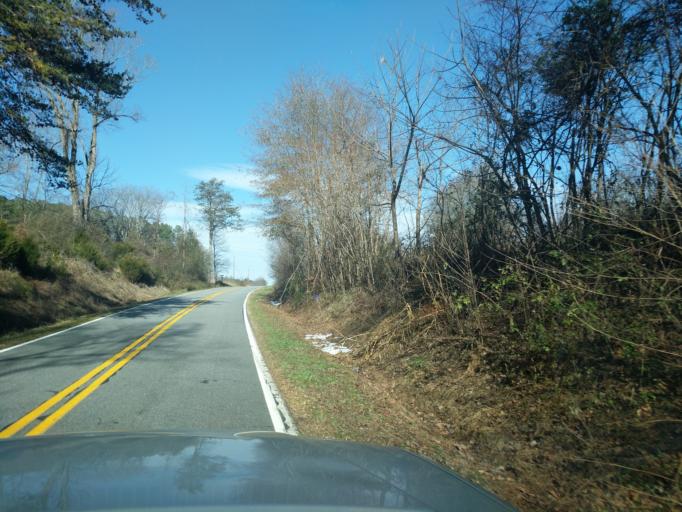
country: US
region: North Carolina
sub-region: McDowell County
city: West Marion
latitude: 35.5838
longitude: -81.9796
